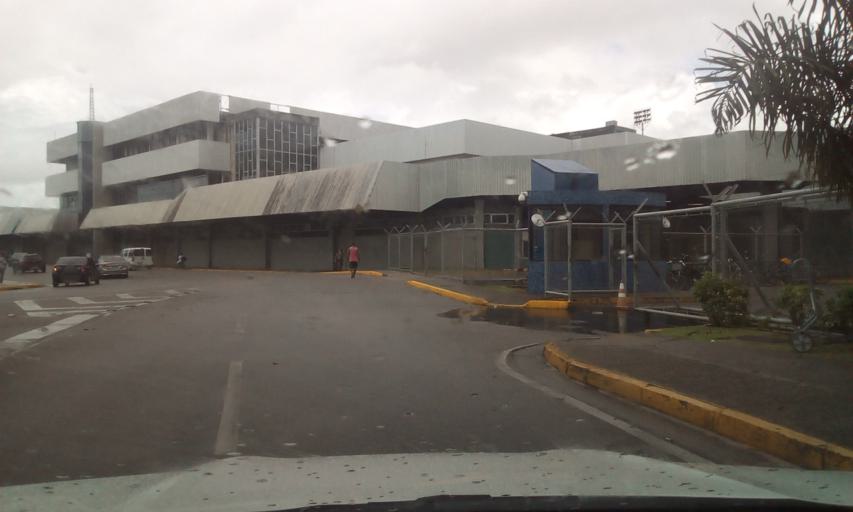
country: BR
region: Pernambuco
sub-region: Recife
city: Recife
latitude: -8.1328
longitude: -34.9176
